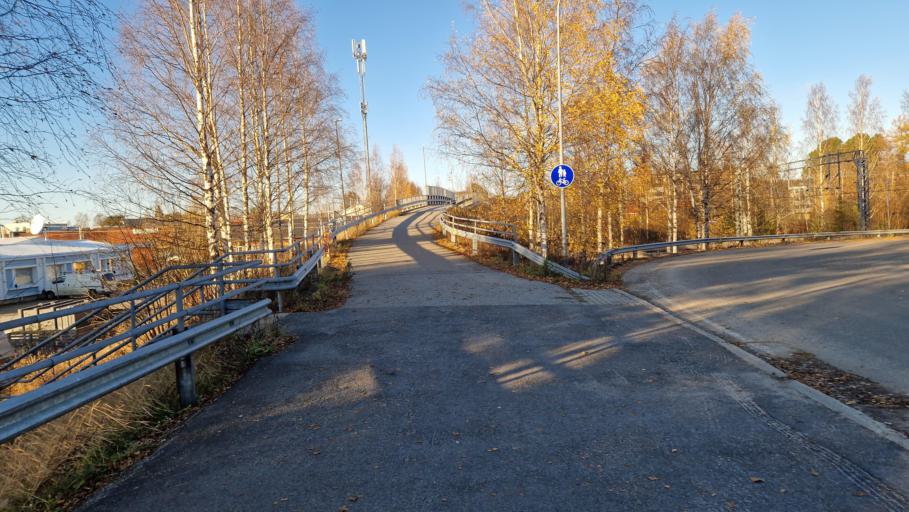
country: FI
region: Kainuu
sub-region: Kajaani
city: Kajaani
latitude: 64.2189
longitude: 27.7347
